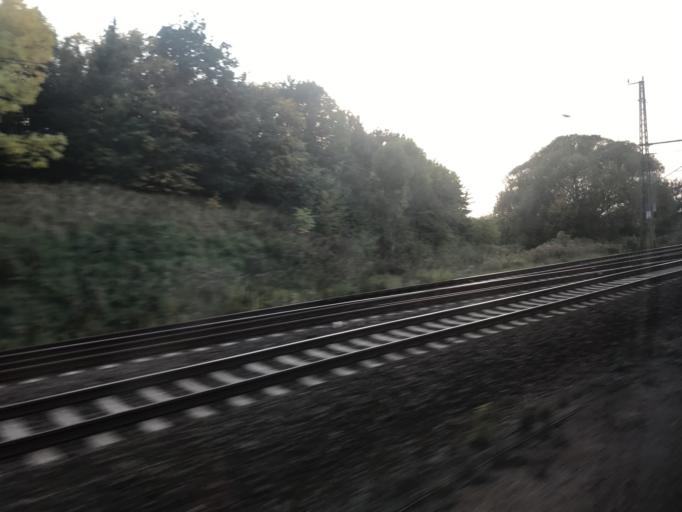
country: DE
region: Saxony
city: Schkeuditz
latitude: 51.3914
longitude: 12.2893
